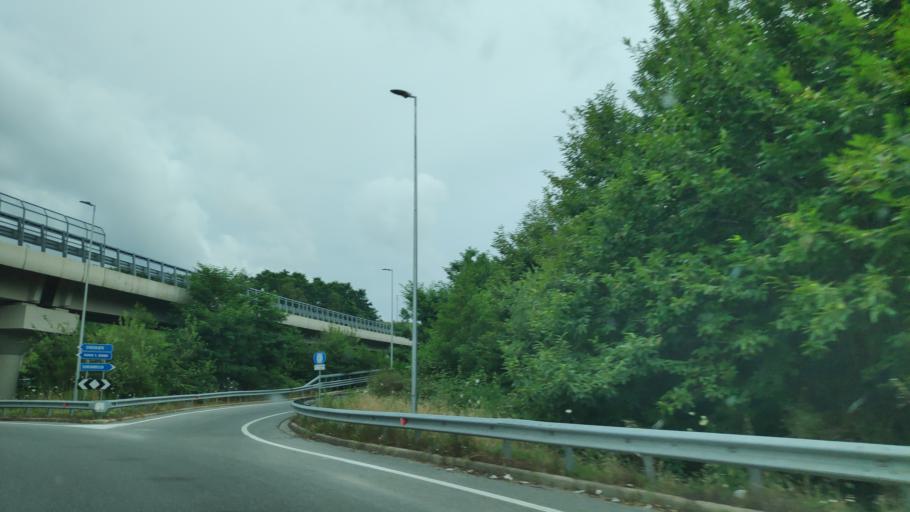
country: IT
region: Calabria
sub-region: Provincia di Vibo-Valentia
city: Spadola
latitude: 38.5925
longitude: 16.3308
